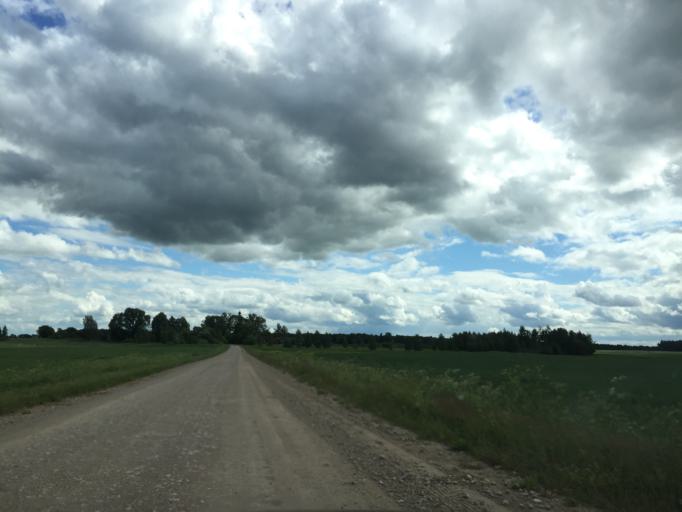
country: LV
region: Vecumnieki
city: Vecumnieki
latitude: 56.4761
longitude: 24.4181
